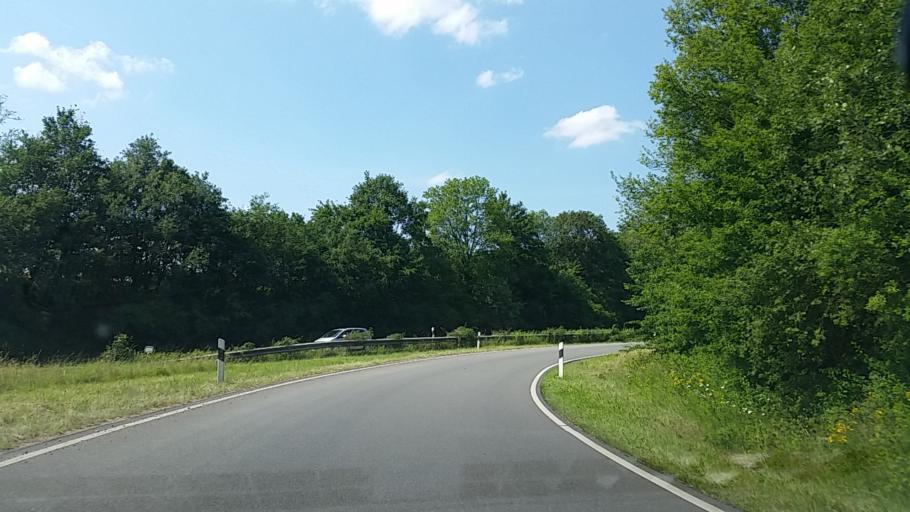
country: DE
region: Schleswig-Holstein
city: Reinbek
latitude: 53.5471
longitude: 10.2374
